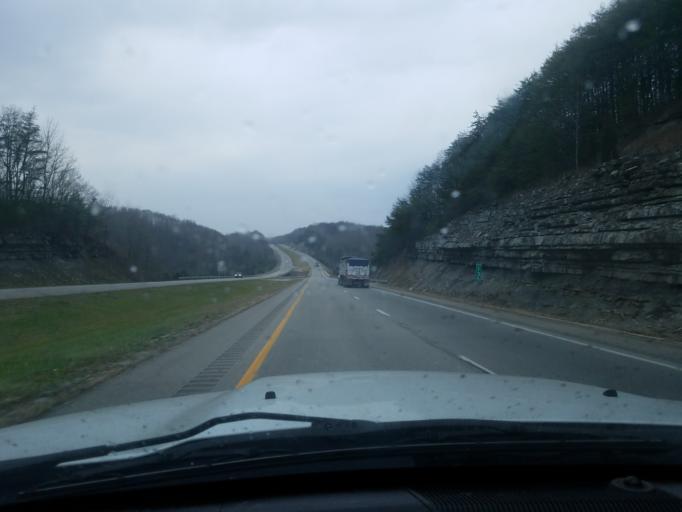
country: US
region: Kentucky
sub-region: Rowan County
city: Morehead
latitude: 38.1860
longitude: -83.5195
